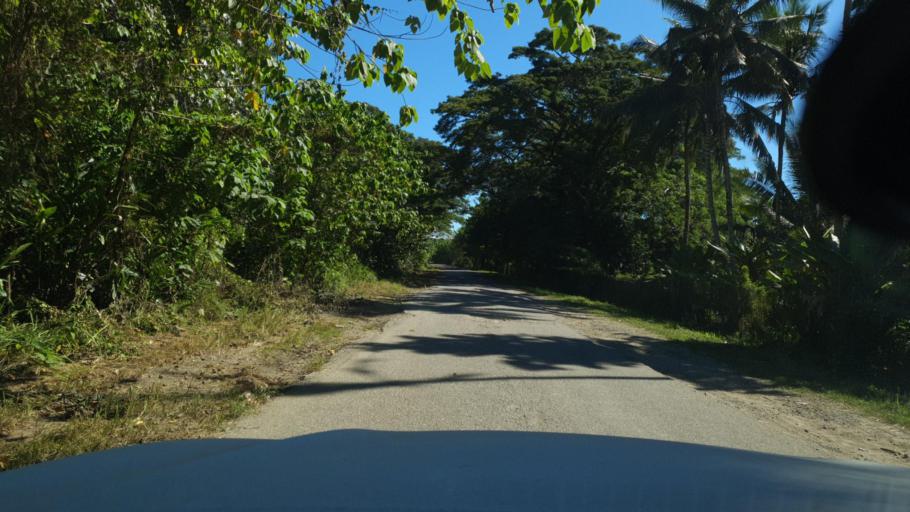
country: SB
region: Guadalcanal
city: Honiara
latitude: -9.3331
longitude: 159.8146
